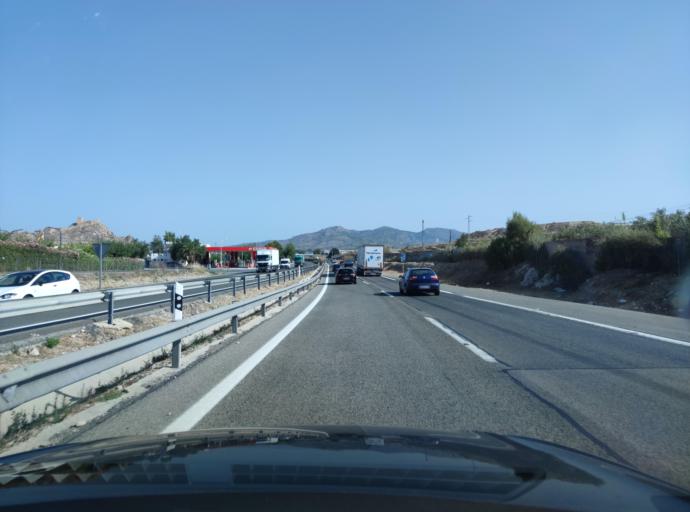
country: ES
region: Valencia
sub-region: Provincia de Alicante
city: Sax
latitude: 38.5308
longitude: -0.8075
